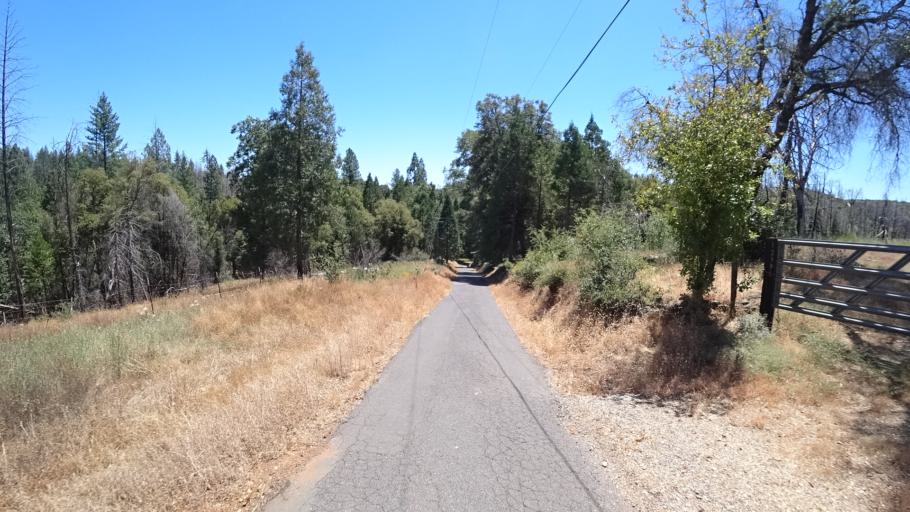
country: US
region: California
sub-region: Calaveras County
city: Mountain Ranch
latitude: 38.2759
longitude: -120.5925
